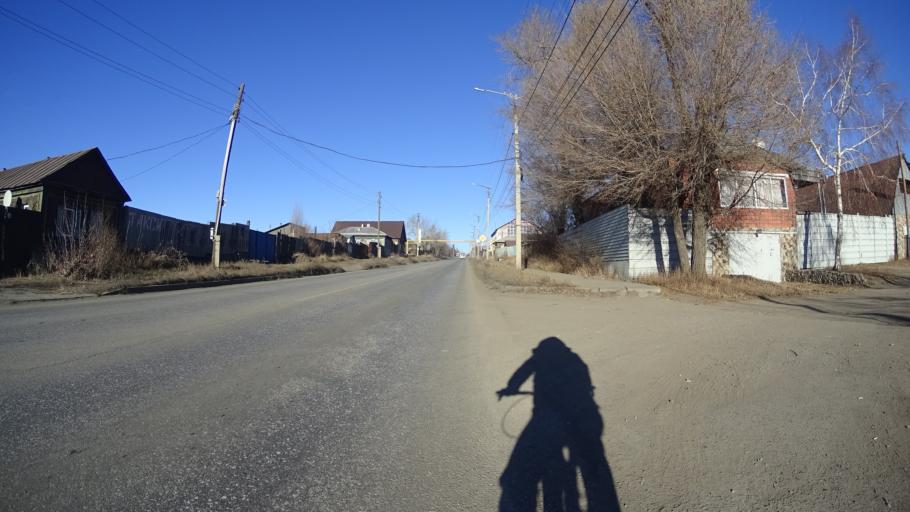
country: RU
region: Chelyabinsk
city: Troitsk
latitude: 54.0992
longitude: 61.5627
